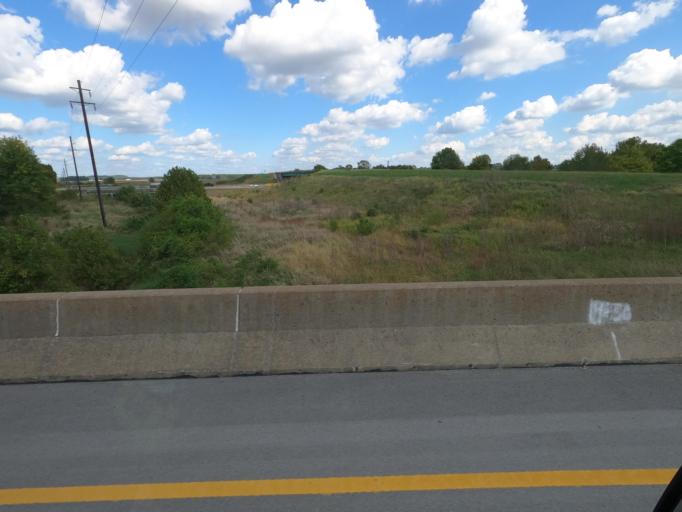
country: US
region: Illinois
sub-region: Massac County
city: Metropolis
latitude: 37.3005
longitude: -88.7551
